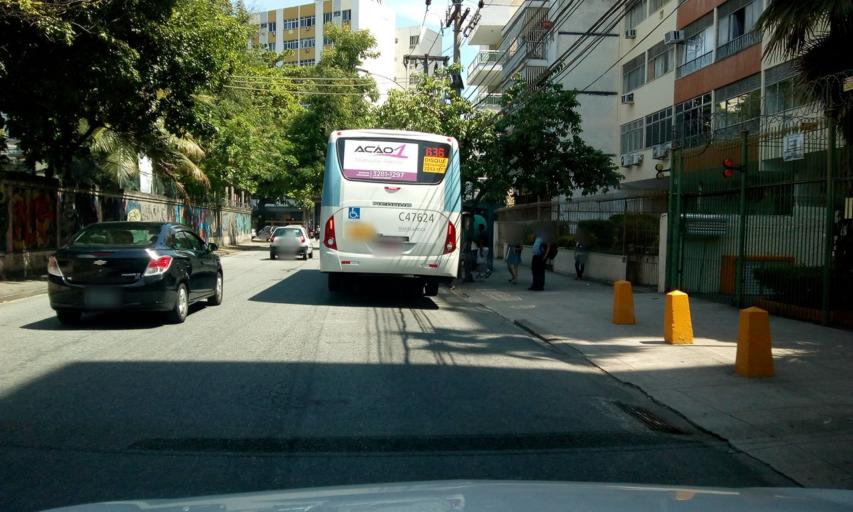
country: BR
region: Rio de Janeiro
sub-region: Rio De Janeiro
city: Rio de Janeiro
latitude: -22.9183
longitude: -43.2629
